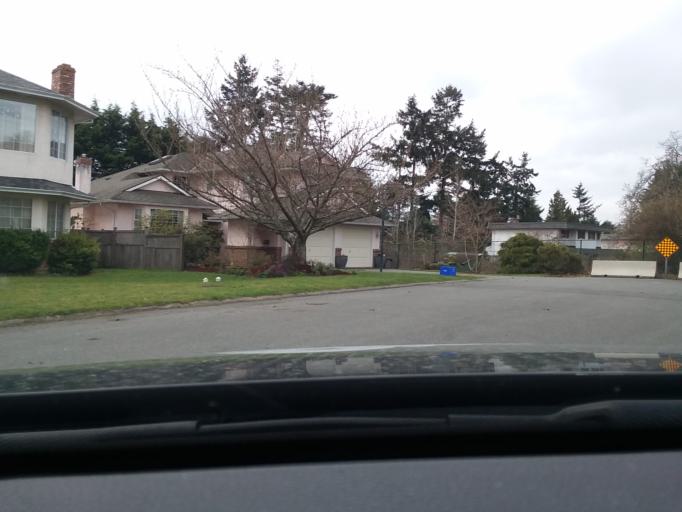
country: CA
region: British Columbia
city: Oak Bay
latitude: 48.4751
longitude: -123.3277
